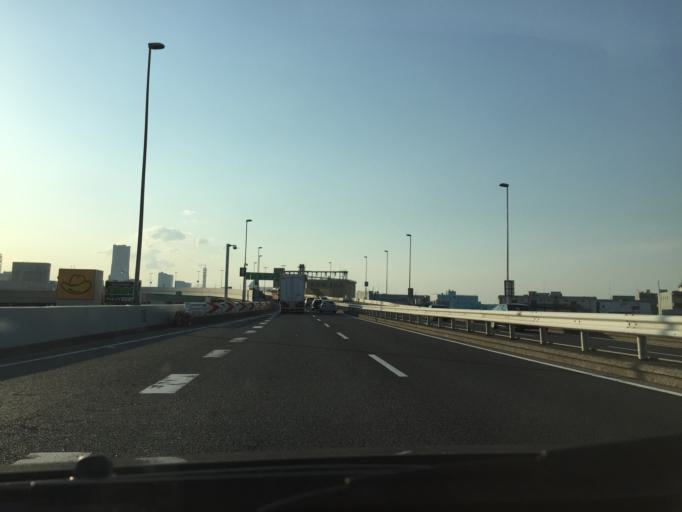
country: JP
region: Kanagawa
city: Yokohama
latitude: 35.4415
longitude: 139.6593
